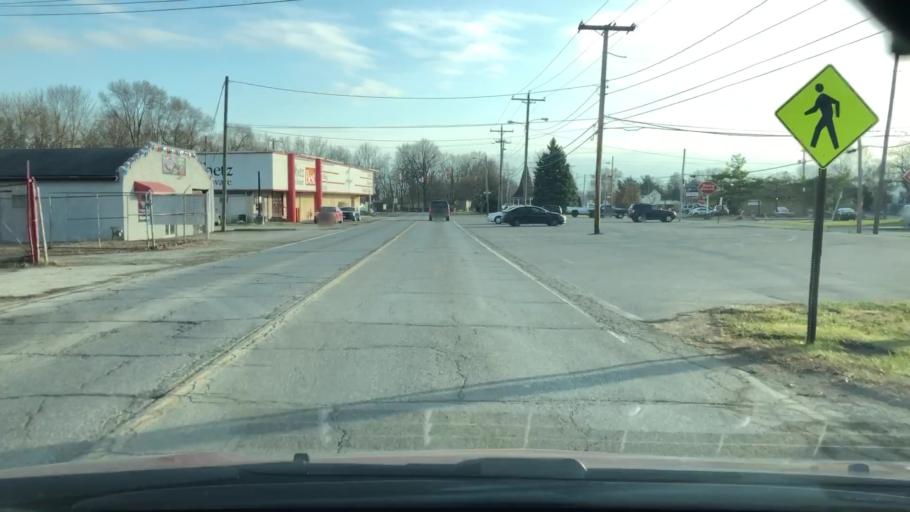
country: US
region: Ohio
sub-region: Franklin County
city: Obetz
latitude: 39.8806
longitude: -82.9510
